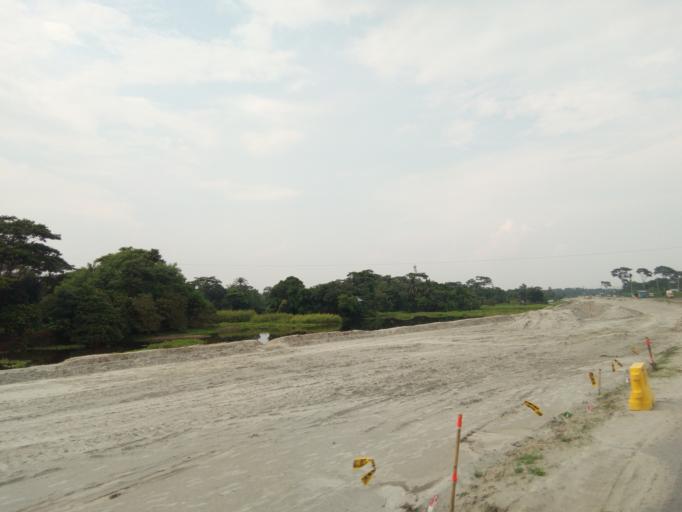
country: BD
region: Dhaka
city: Dohar
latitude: 23.5740
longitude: 90.3040
